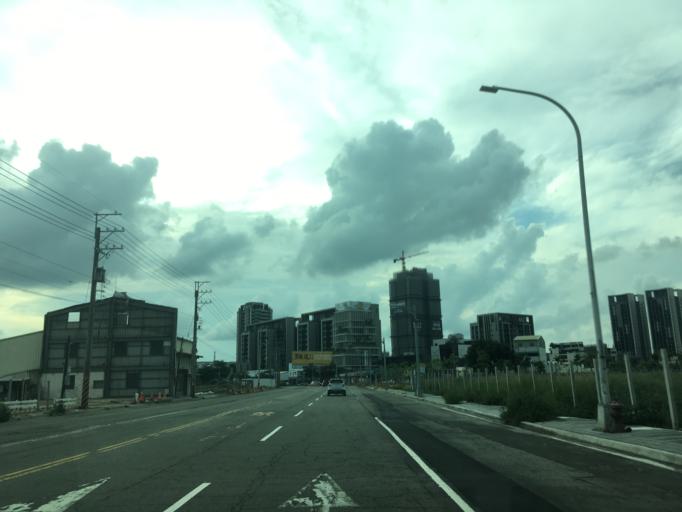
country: TW
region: Taiwan
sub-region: Taichung City
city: Taichung
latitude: 24.1390
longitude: 120.6306
